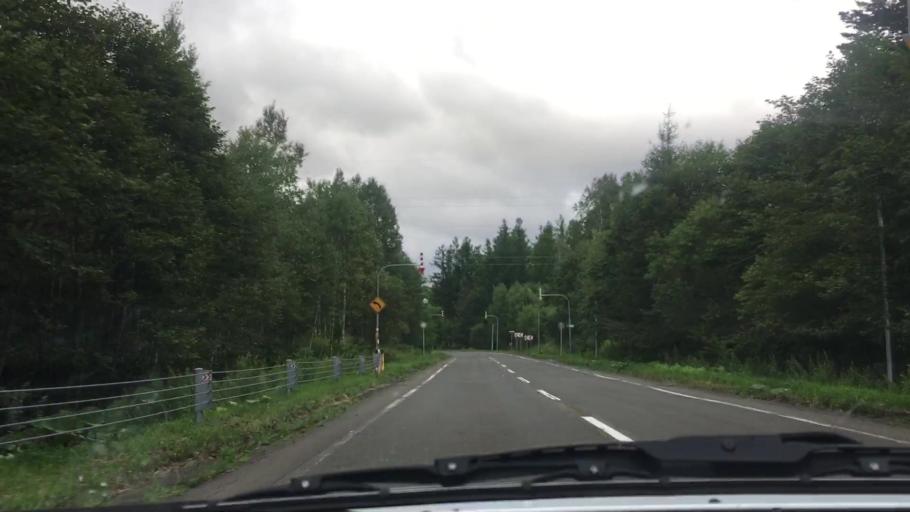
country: JP
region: Hokkaido
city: Shimo-furano
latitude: 43.0558
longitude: 142.6685
